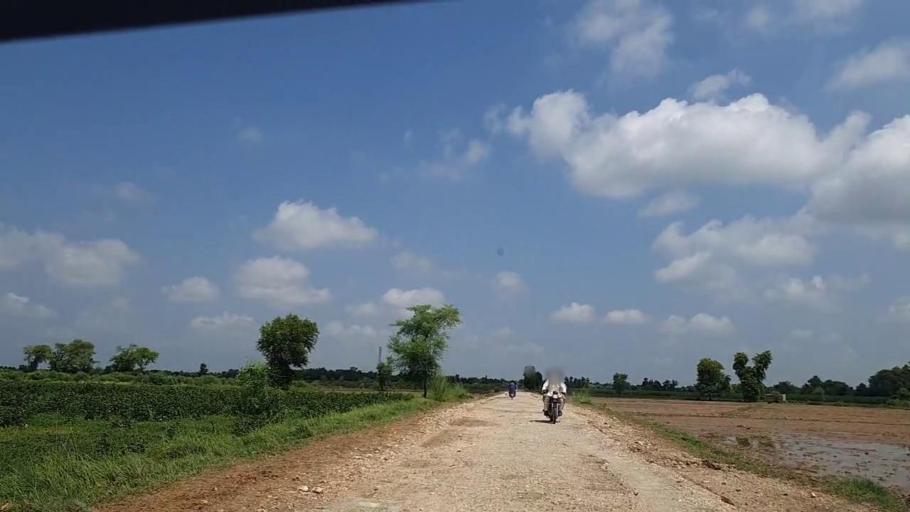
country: PK
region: Sindh
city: Tharu Shah
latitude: 26.9031
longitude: 68.0386
